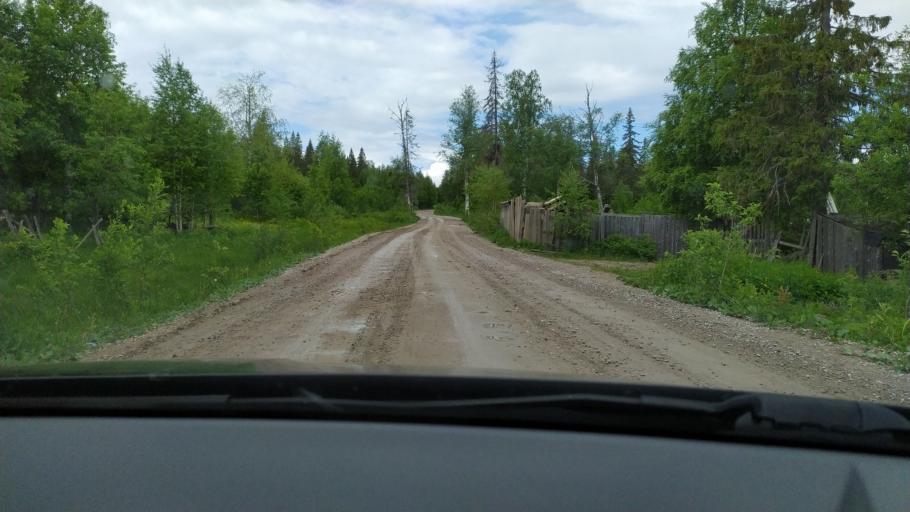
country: RU
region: Perm
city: Gremyachinsk
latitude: 58.5105
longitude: 57.8211
